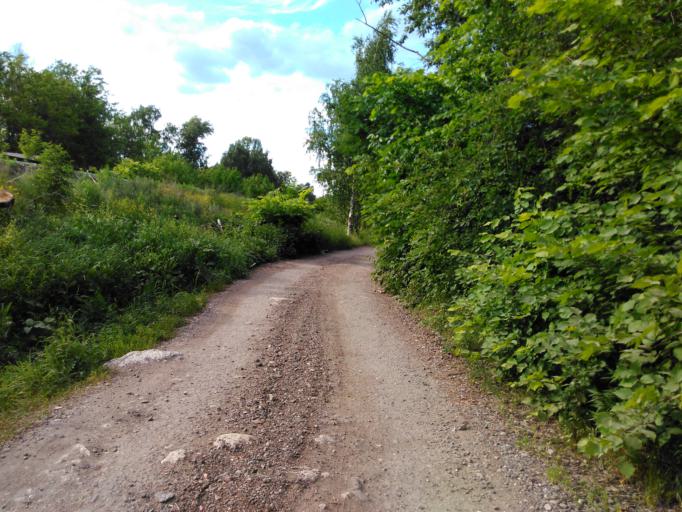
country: RU
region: Moskovskaya
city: Vishnyakovskiye Dachi
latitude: 55.7594
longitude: 38.1418
